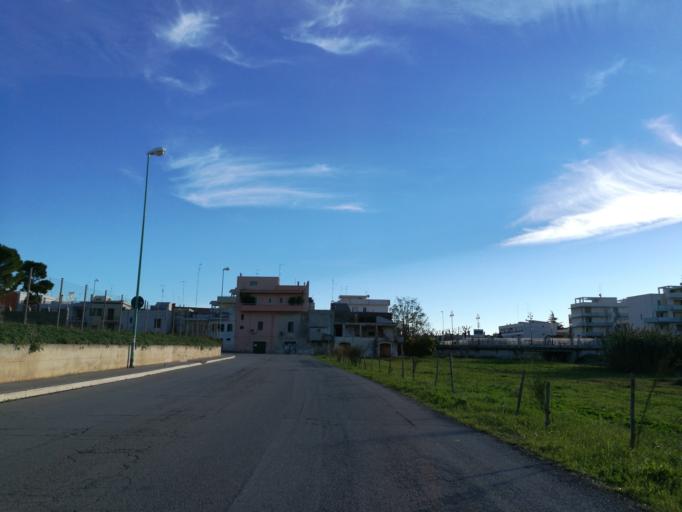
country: IT
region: Apulia
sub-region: Provincia di Bari
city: Adelfia
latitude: 41.0050
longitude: 16.8739
